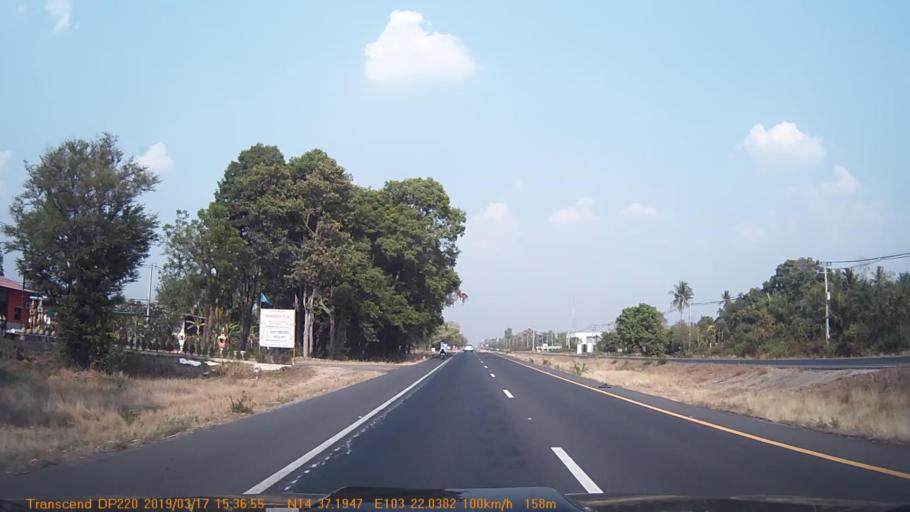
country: TH
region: Surin
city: Prasat
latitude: 14.6200
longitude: 103.3678
